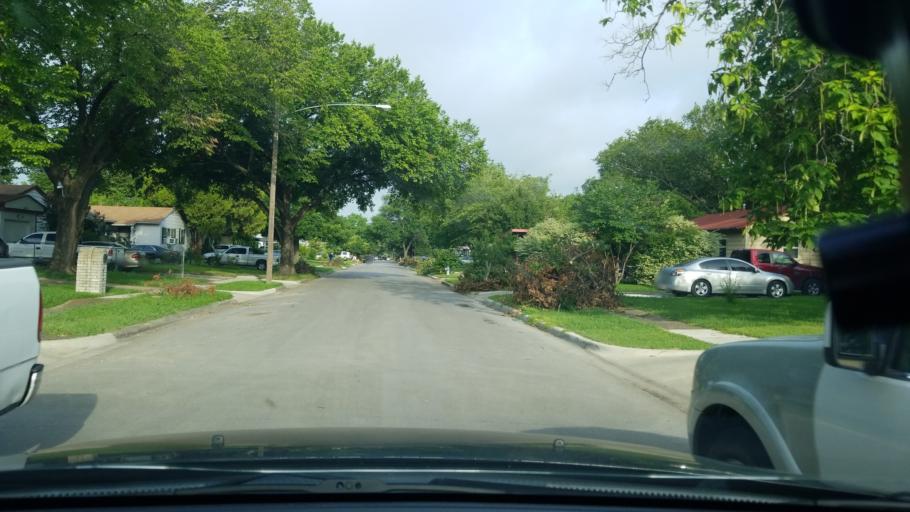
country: US
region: Texas
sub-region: Dallas County
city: Garland
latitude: 32.8277
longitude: -96.6653
